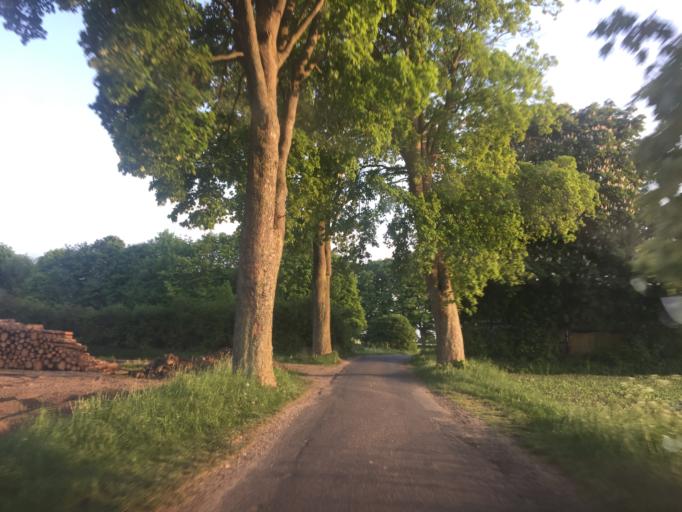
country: DK
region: South Denmark
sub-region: Kerteminde Kommune
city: Langeskov
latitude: 55.3477
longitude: 10.5237
